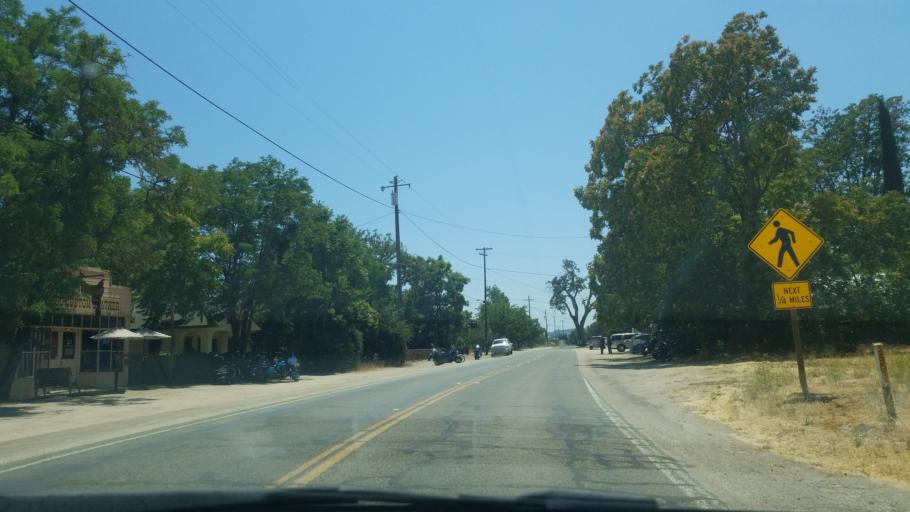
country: US
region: California
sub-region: San Luis Obispo County
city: Atascadero
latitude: 35.5202
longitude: -120.5235
